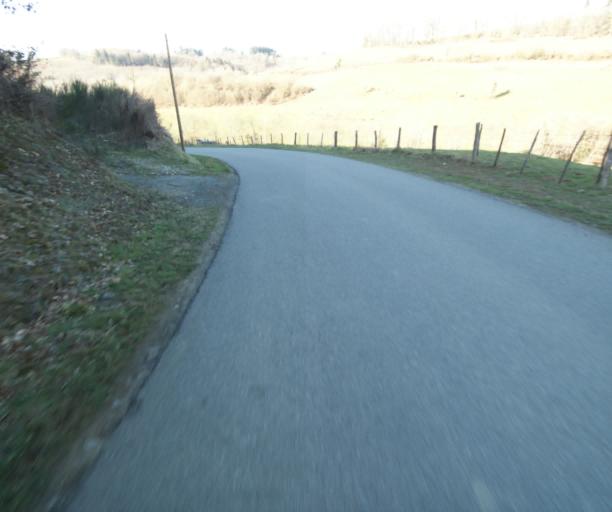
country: FR
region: Limousin
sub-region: Departement de la Correze
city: Seilhac
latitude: 45.3816
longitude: 1.7502
